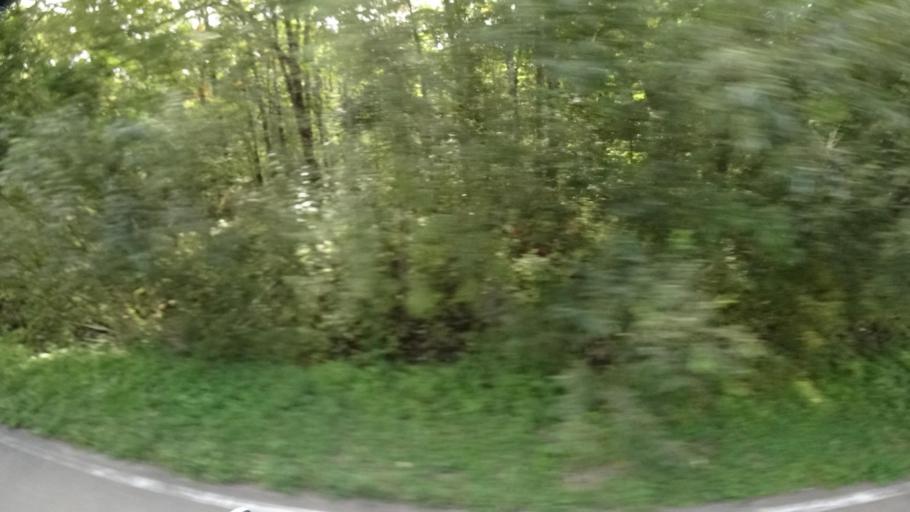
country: RU
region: Primorskiy
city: Yakovlevka
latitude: 44.4016
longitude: 133.5961
